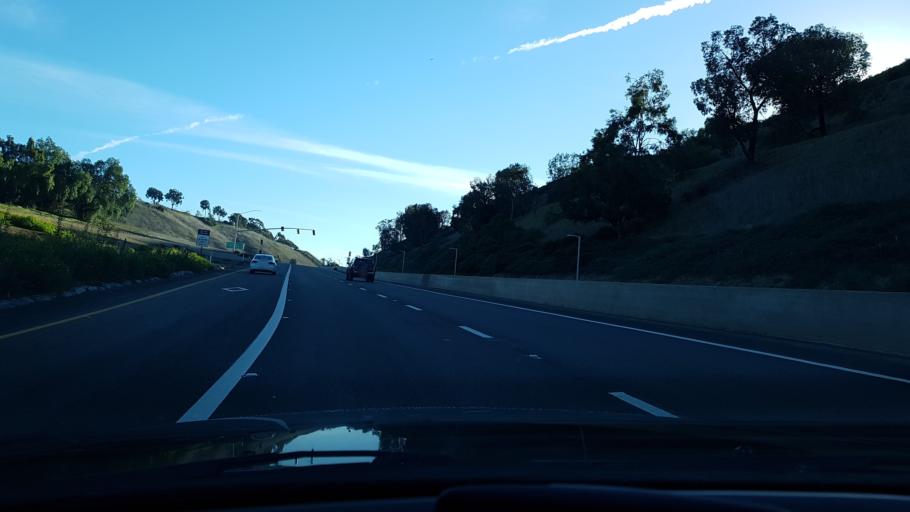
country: US
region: California
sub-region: San Diego County
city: Del Mar
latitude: 32.9004
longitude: -117.2256
